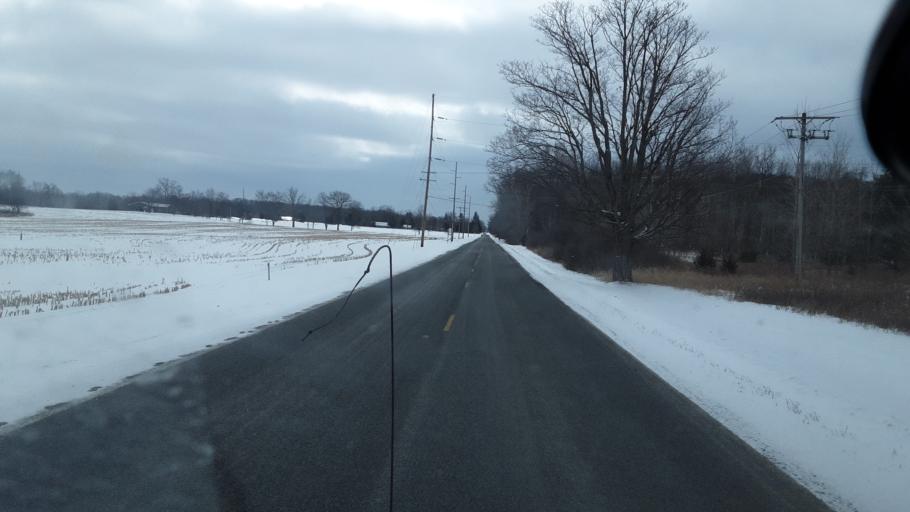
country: US
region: Michigan
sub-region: Ingham County
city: Holt
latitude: 42.6146
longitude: -84.5429
